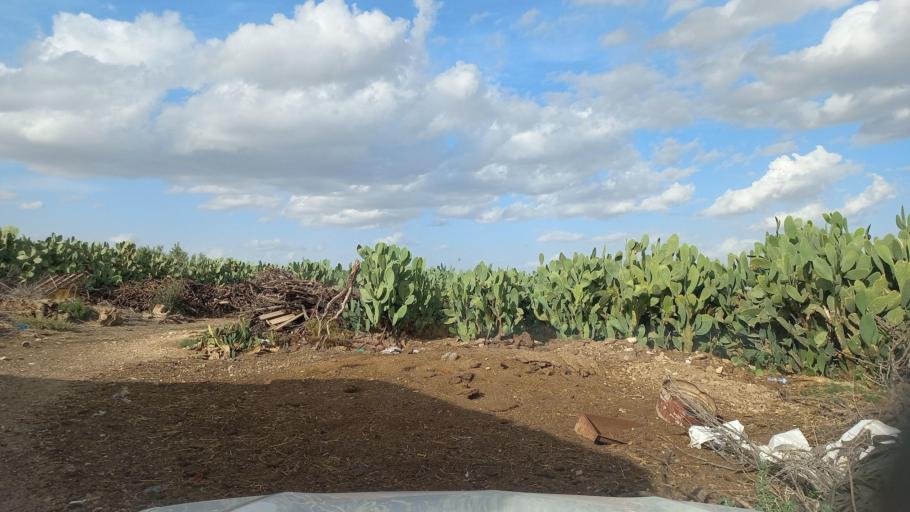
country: TN
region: Al Qasrayn
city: Sbiba
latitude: 35.4478
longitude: 9.0778
